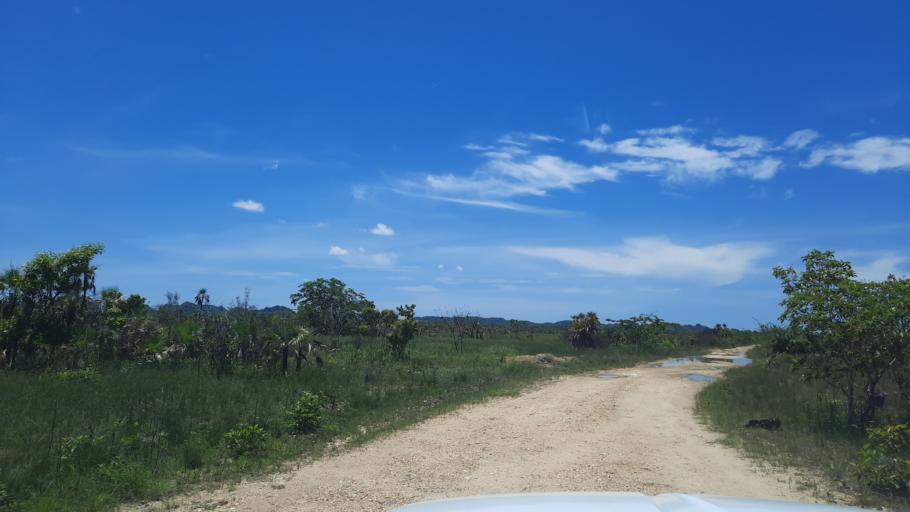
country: BZ
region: Cayo
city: Belmopan
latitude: 17.3846
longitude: -88.4948
